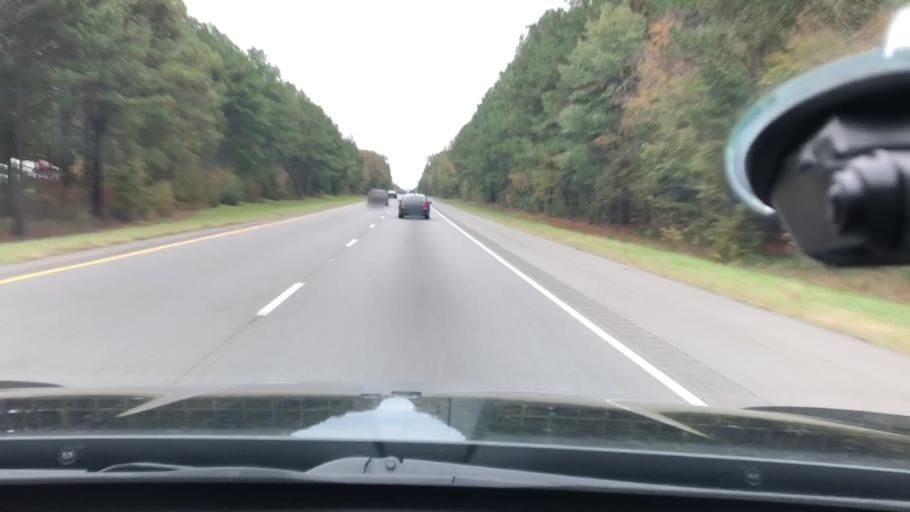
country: US
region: Arkansas
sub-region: Hempstead County
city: Hope
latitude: 33.6358
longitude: -93.7097
